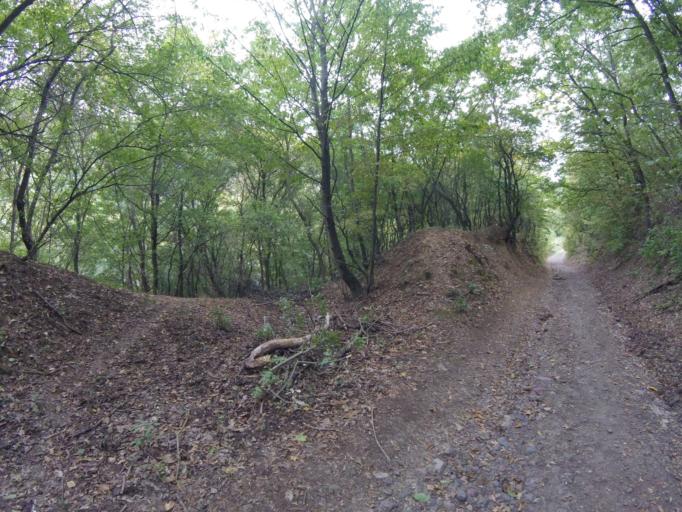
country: HU
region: Pest
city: Szob
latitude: 47.8318
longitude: 18.8125
